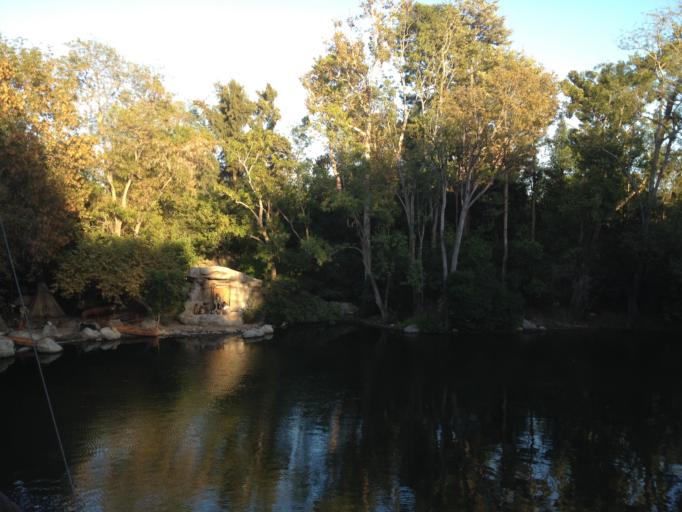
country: US
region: California
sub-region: Orange County
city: Anaheim
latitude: 33.8140
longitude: -117.9215
